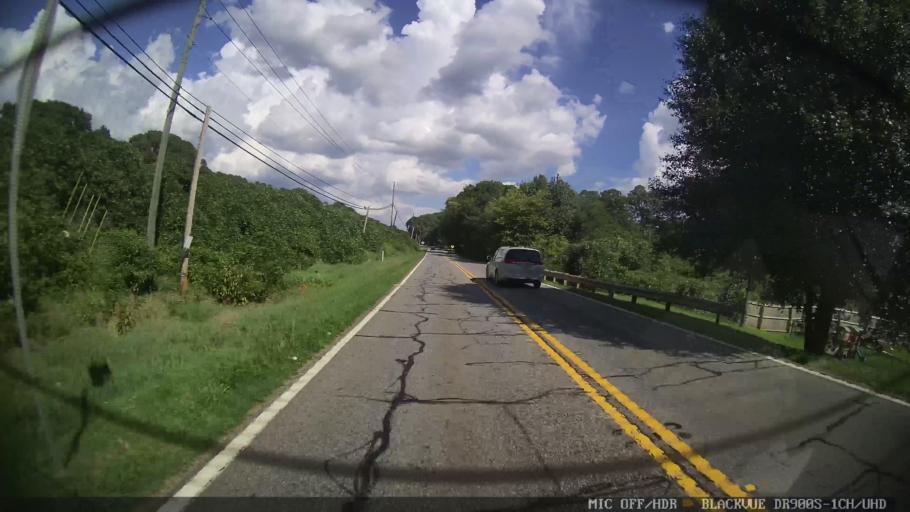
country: US
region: Georgia
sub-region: Bartow County
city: Emerson
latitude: 34.1316
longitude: -84.7578
